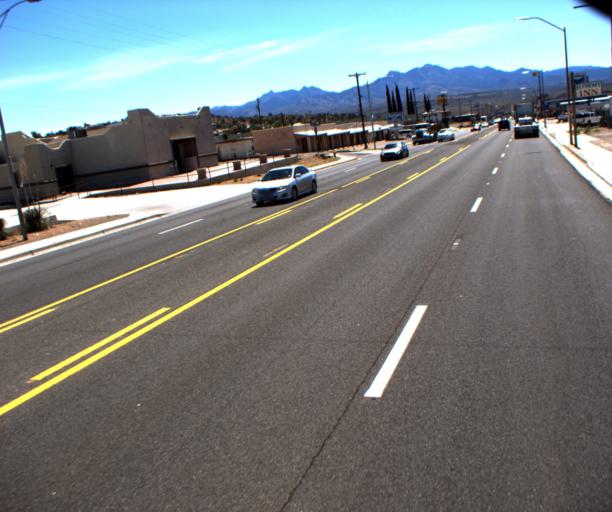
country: US
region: Arizona
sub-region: Mohave County
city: Kingman
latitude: 35.1974
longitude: -114.0767
